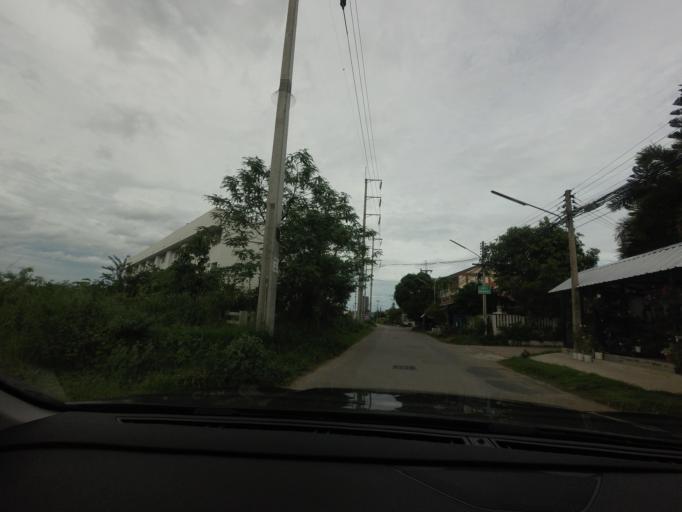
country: TH
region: Prachuap Khiri Khan
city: Hua Hin
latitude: 12.5372
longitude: 99.9480
